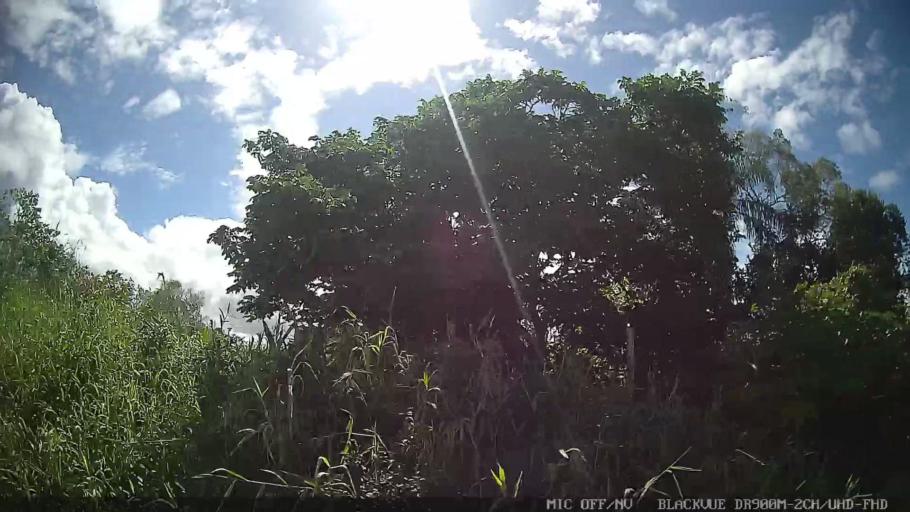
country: BR
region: Sao Paulo
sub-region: Itanhaem
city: Itanhaem
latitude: -24.2226
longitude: -46.8661
